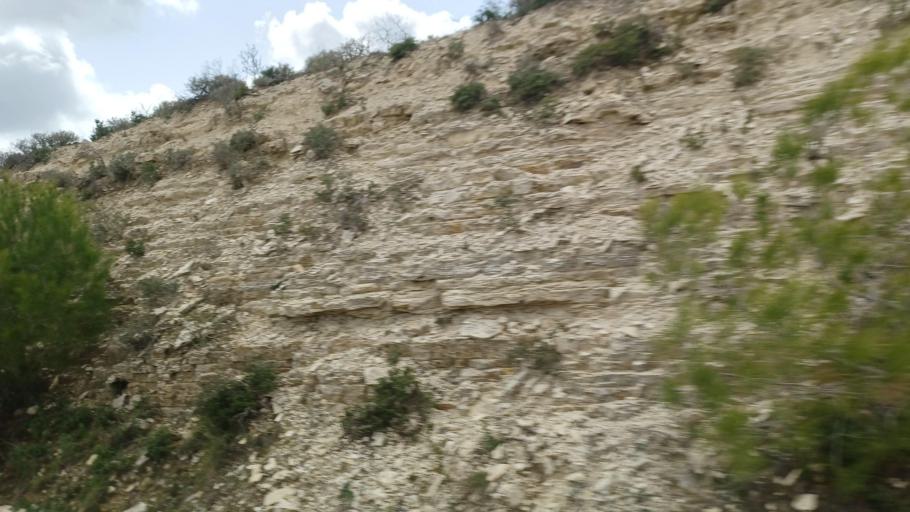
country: CY
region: Limassol
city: Pachna
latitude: 34.8210
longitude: 32.7723
